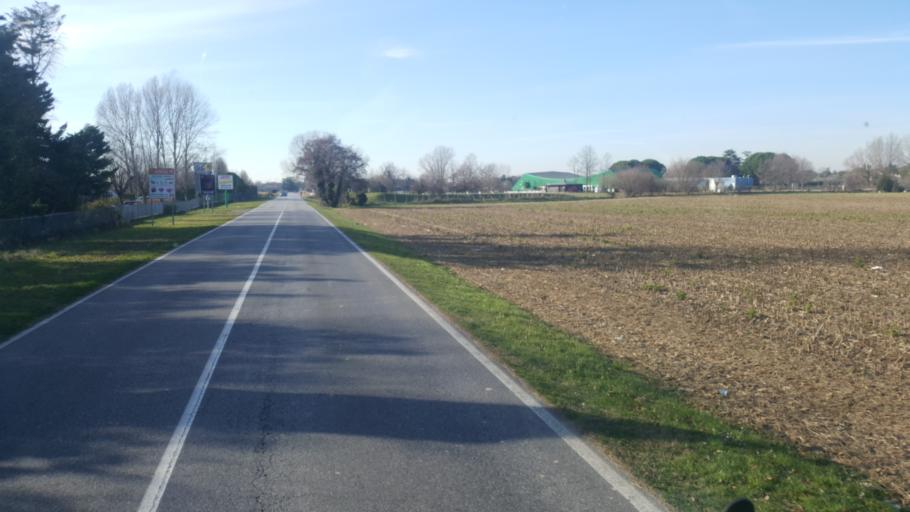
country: IT
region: Friuli Venezia Giulia
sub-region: Provincia di Gorizia
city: Staranzano
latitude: 45.7964
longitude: 13.5157
